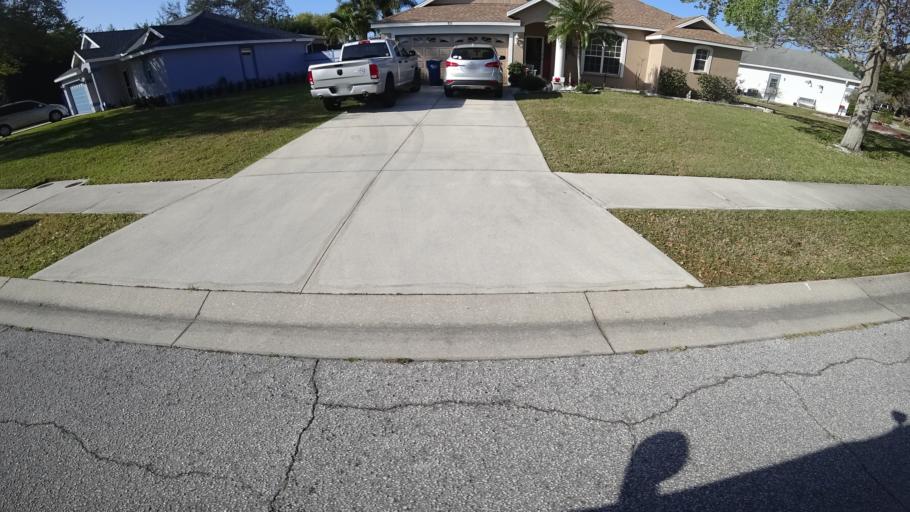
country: US
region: Florida
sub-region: Manatee County
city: Whitfield
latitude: 27.4127
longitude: -82.5579
